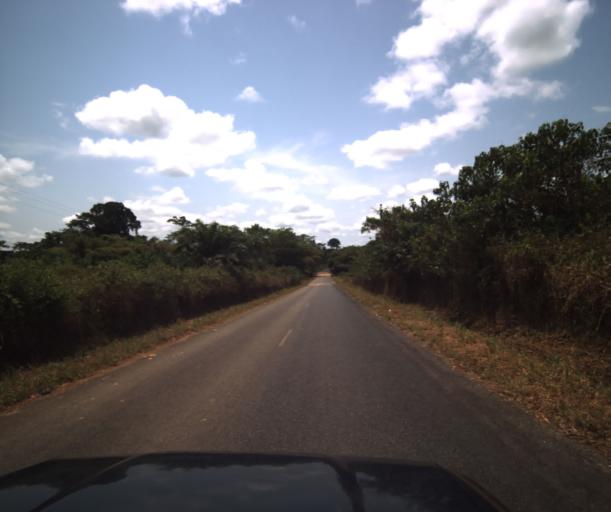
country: CM
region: Centre
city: Eseka
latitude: 3.7095
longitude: 10.7942
